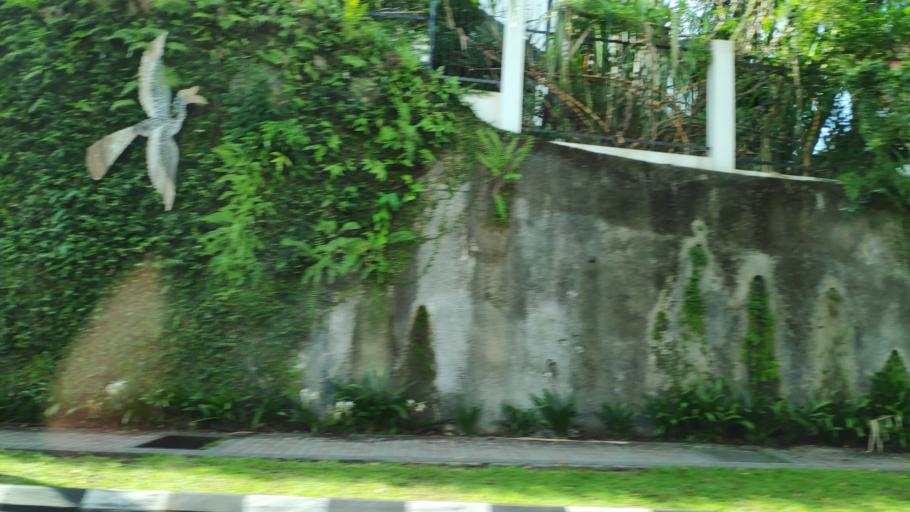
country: MY
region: Sarawak
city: Kuching
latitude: 1.5575
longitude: 110.3472
